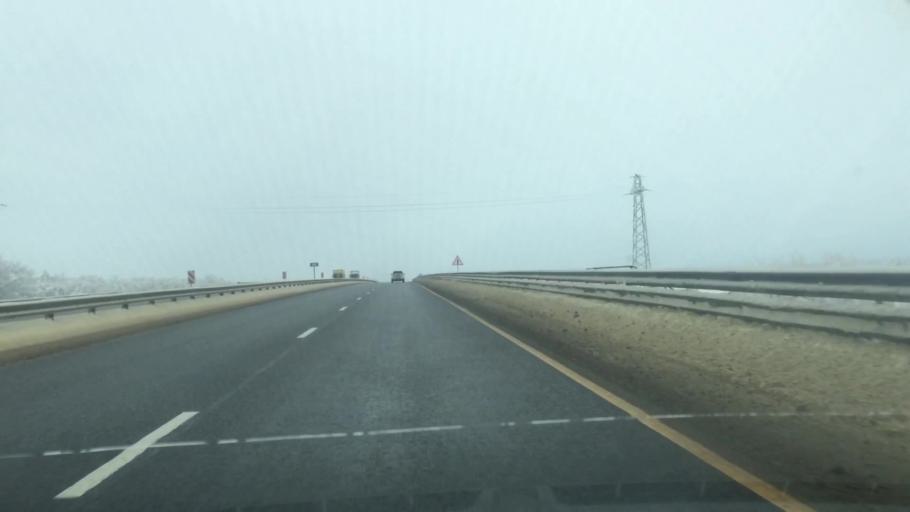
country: RU
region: Lipetsk
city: Zadonsk
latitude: 52.5064
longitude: 38.7557
